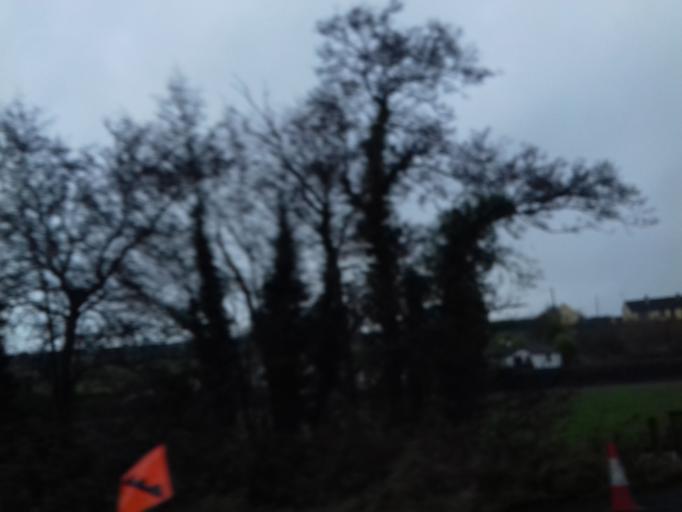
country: IE
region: Ulster
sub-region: County Donegal
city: Raphoe
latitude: 54.9392
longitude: -7.6173
